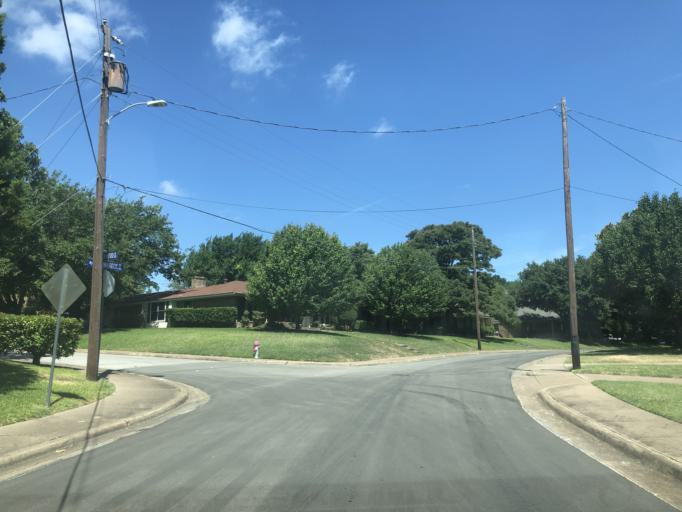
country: US
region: Texas
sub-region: Dallas County
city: Duncanville
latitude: 32.6483
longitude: -96.9194
